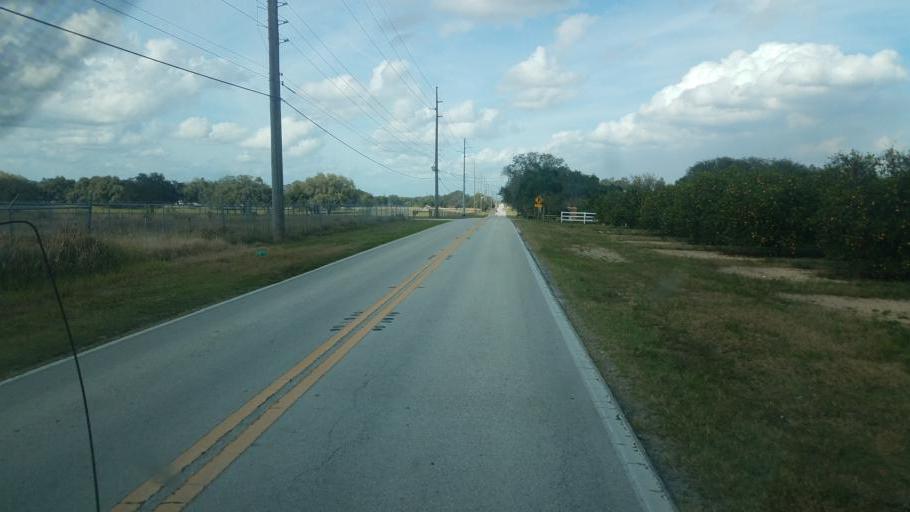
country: US
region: Florida
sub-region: Polk County
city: Haines City
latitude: 28.1260
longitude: -81.5904
